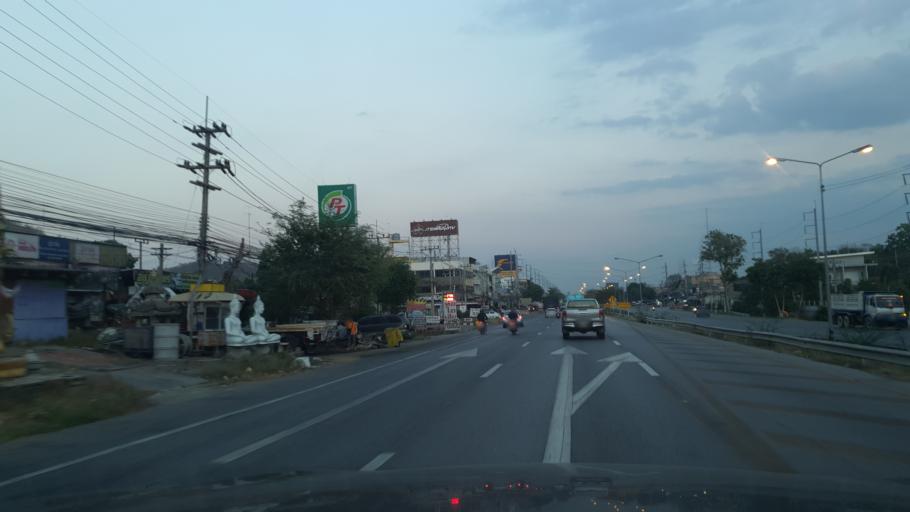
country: TH
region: Nakhon Sawan
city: Nakhon Sawan
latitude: 15.7071
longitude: 100.1000
